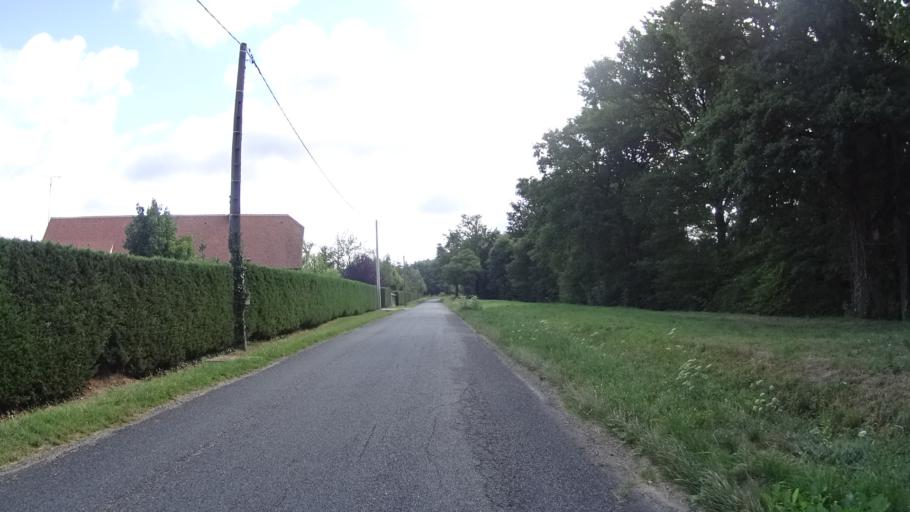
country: FR
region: Centre
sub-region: Departement du Loiret
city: Lorris
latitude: 47.8923
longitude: 2.4550
